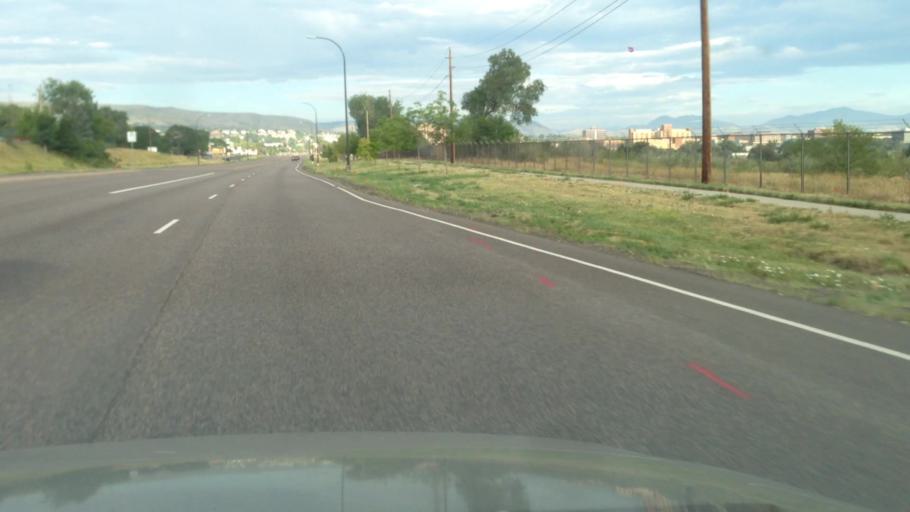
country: US
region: Colorado
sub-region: Jefferson County
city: Lakewood
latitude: 39.7111
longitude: -105.1117
